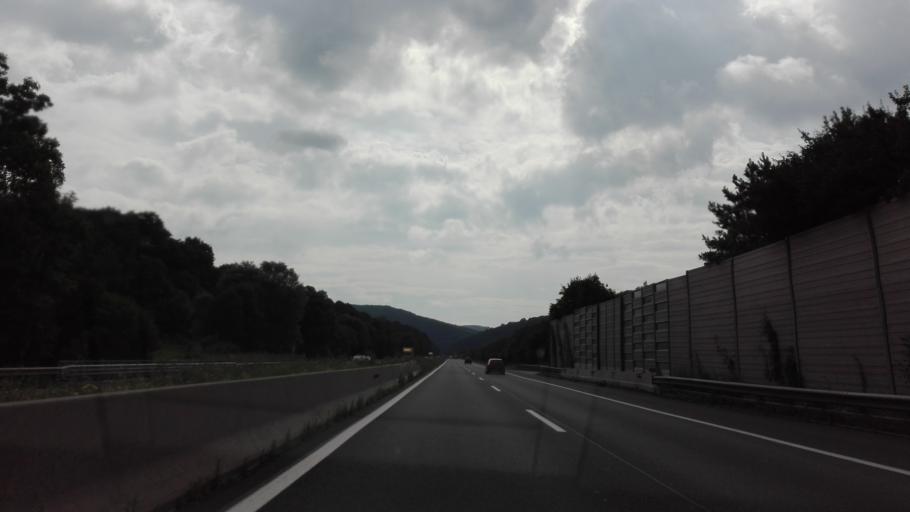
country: AT
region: Lower Austria
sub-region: Politischer Bezirk Baden
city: Klausen-Leopoldsdorf
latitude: 48.0858
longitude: 16.0226
